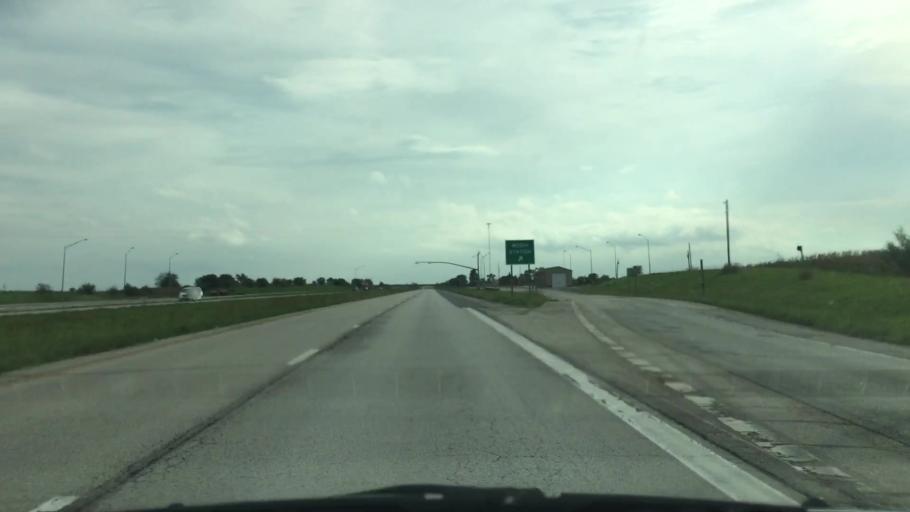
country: US
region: Iowa
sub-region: Decatur County
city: Lamoni
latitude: 40.5242
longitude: -93.9608
